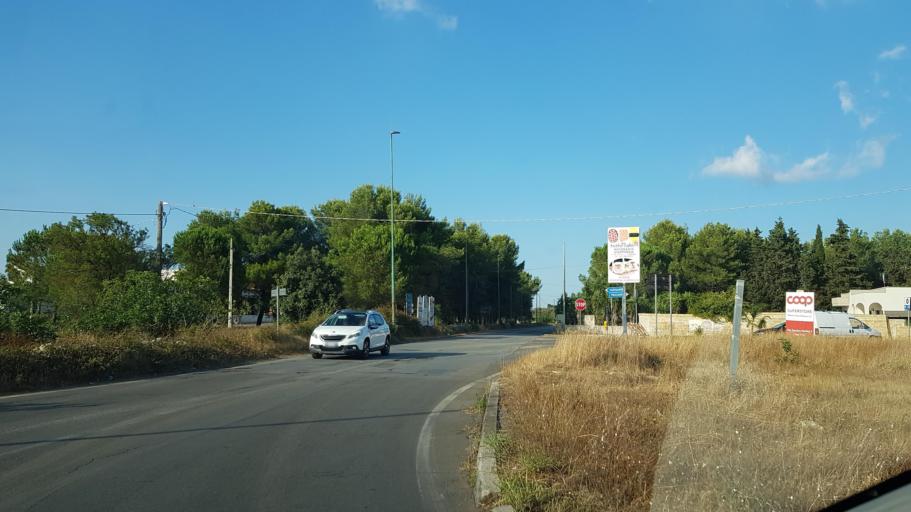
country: IT
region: Apulia
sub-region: Provincia di Lecce
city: Montesano Salentino
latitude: 39.9733
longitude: 18.3263
